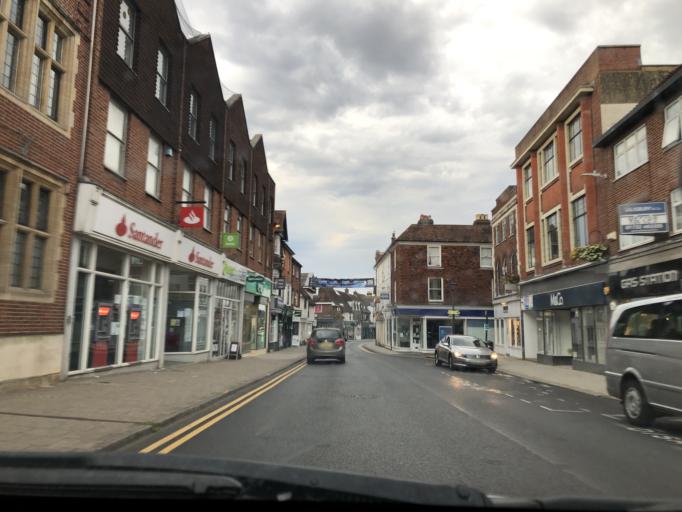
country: GB
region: England
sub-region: Kent
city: Sevenoaks
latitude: 51.2702
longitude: 0.1929
